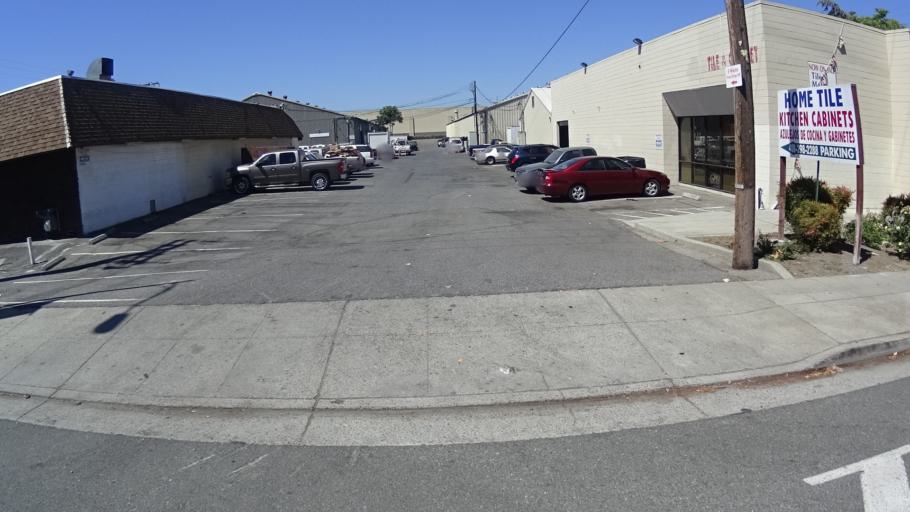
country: US
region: California
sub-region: Santa Clara County
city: Seven Trees
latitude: 37.3062
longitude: -121.8639
